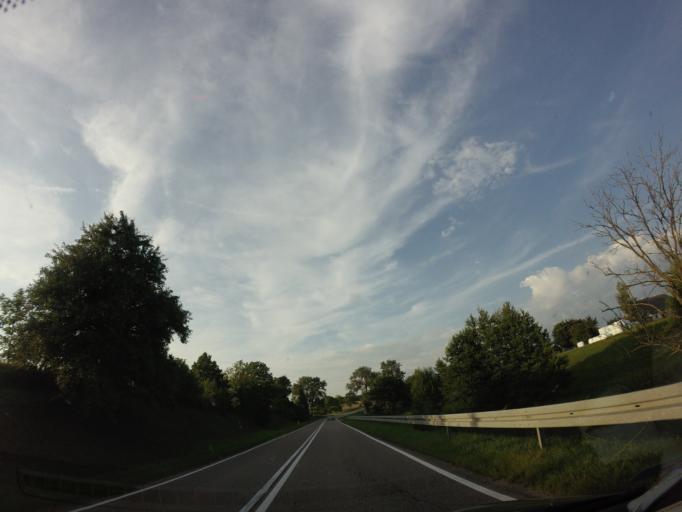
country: PL
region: Podlasie
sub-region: Powiat sejnenski
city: Sejny
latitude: 54.1204
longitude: 23.4304
